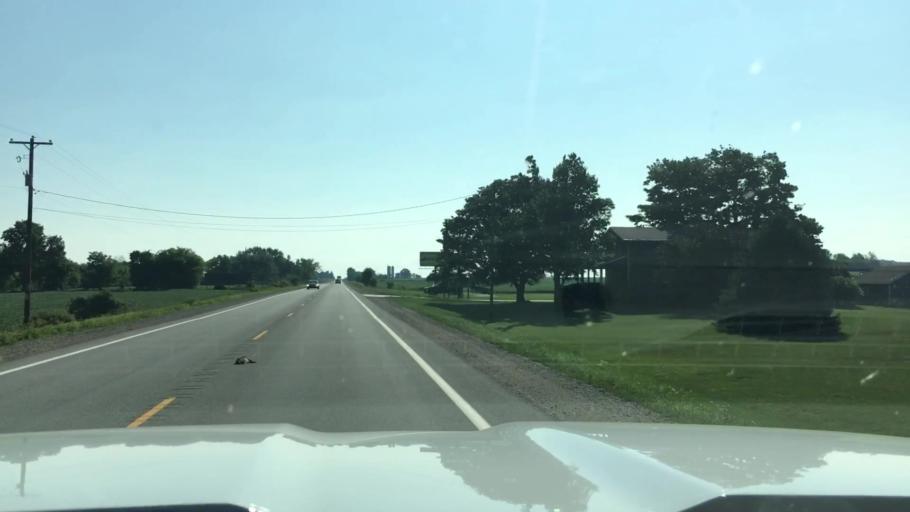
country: US
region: Michigan
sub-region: Gratiot County
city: Ithaca
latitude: 43.1772
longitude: -84.6683
